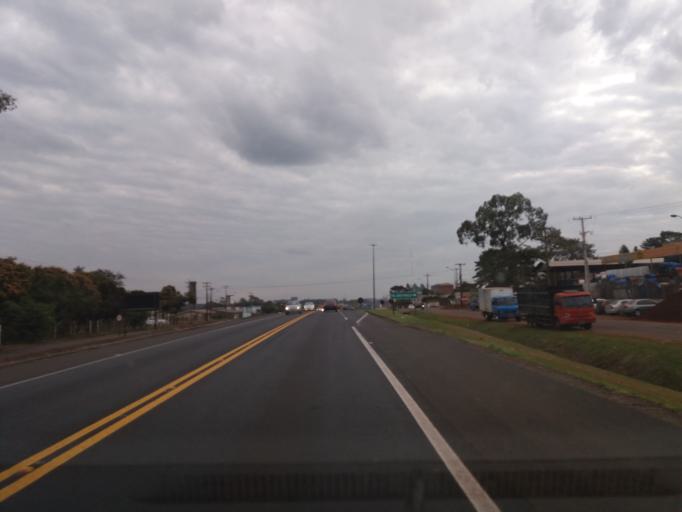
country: BR
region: Parana
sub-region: Cascavel
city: Cascavel
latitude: -24.9839
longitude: -53.4628
